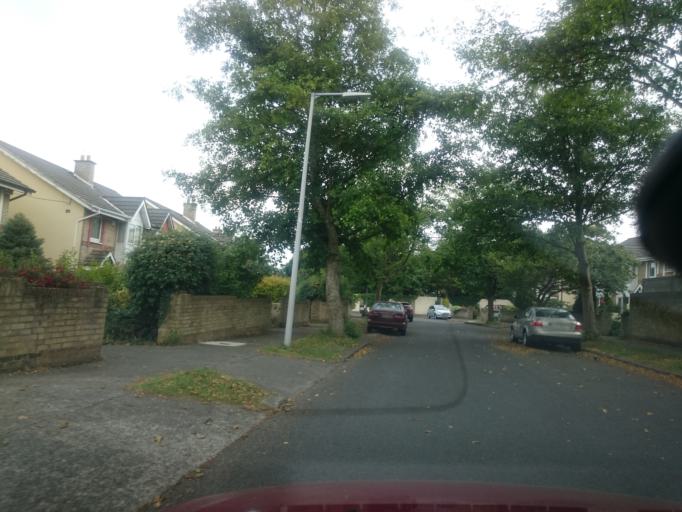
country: IE
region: Leinster
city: Mount Merrion
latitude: 53.3023
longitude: -6.2222
